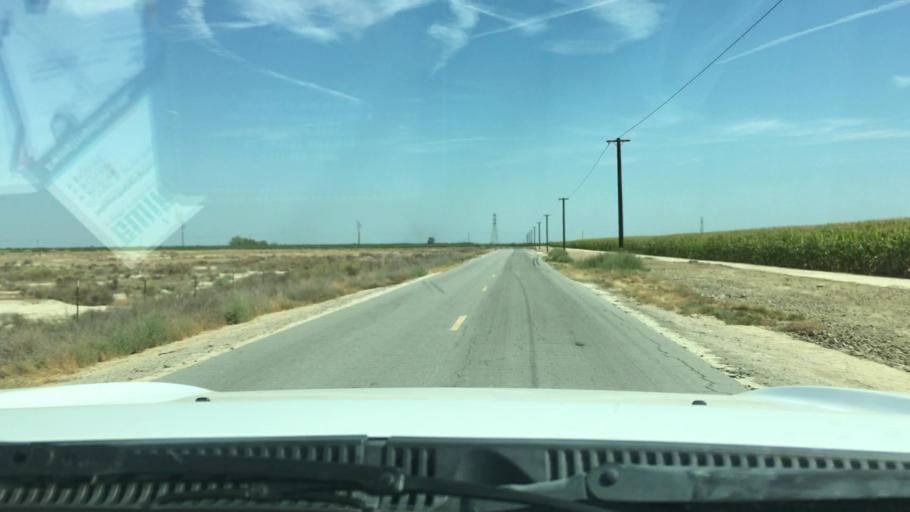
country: US
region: California
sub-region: Kern County
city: Buttonwillow
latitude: 35.4361
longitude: -119.3761
